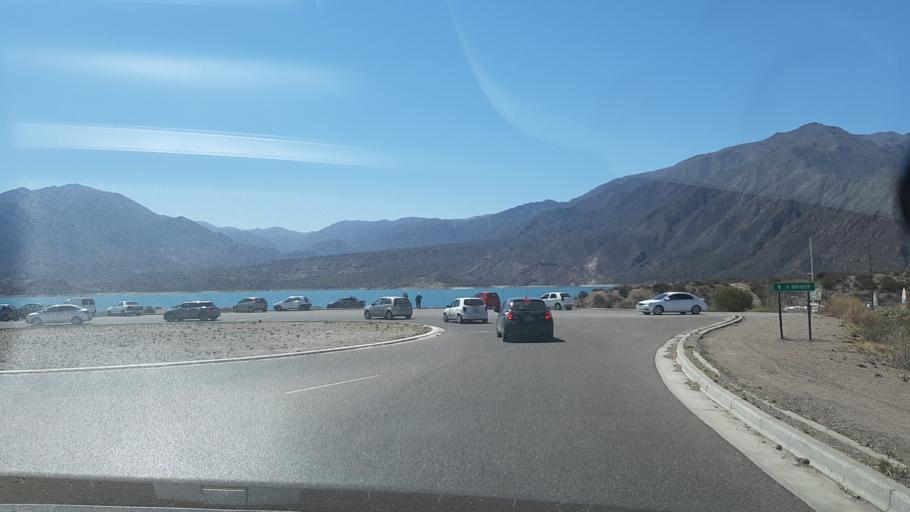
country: AR
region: Mendoza
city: Lujan de Cuyo
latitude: -32.9891
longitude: -69.1661
